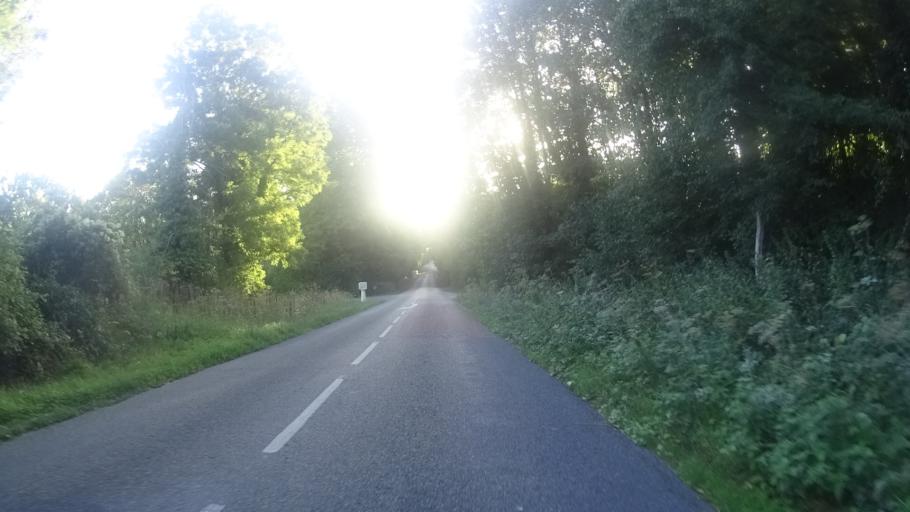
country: FR
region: Picardie
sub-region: Departement de l'Oise
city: Ver-sur-Launette
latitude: 49.1726
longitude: 2.6797
